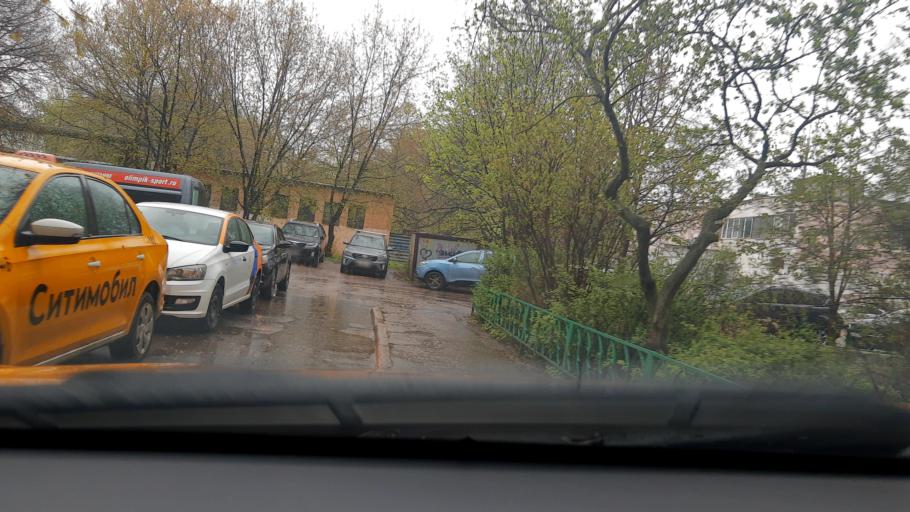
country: RU
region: Moskovskaya
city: Dolgoprudnyy
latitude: 55.9438
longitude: 37.4968
